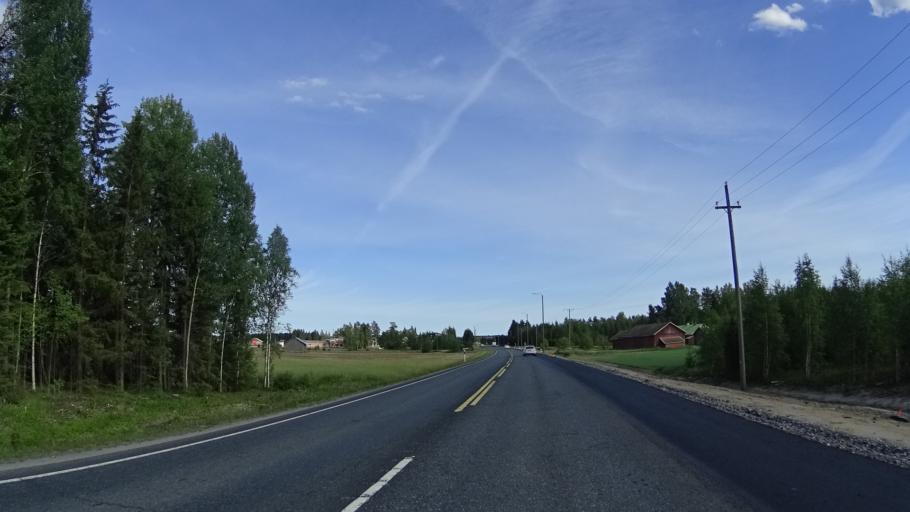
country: FI
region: Haeme
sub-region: Forssa
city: Forssa
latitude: 60.7707
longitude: 23.6789
